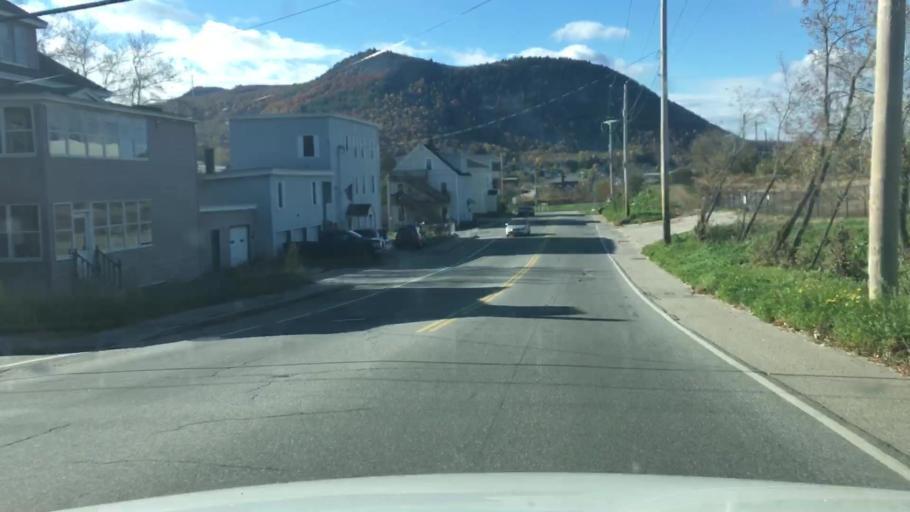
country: US
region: New Hampshire
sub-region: Coos County
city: Berlin
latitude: 44.4693
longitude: -71.1728
